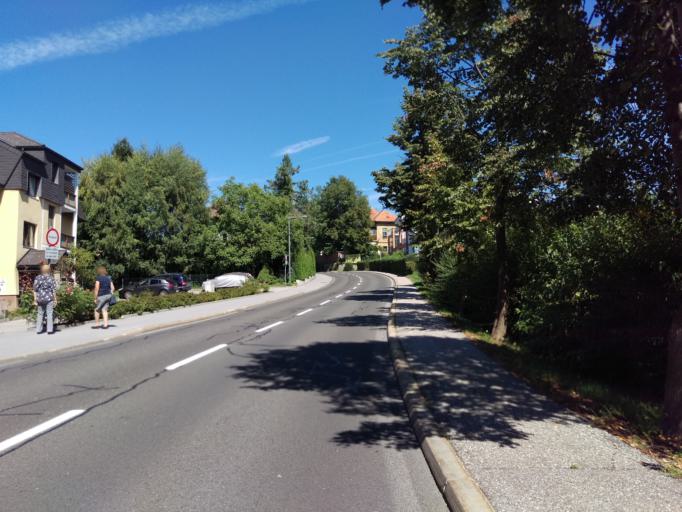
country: AT
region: Styria
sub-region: Politischer Bezirk Graz-Umgebung
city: Nestelbach bei Graz
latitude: 47.0779
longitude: 15.5814
